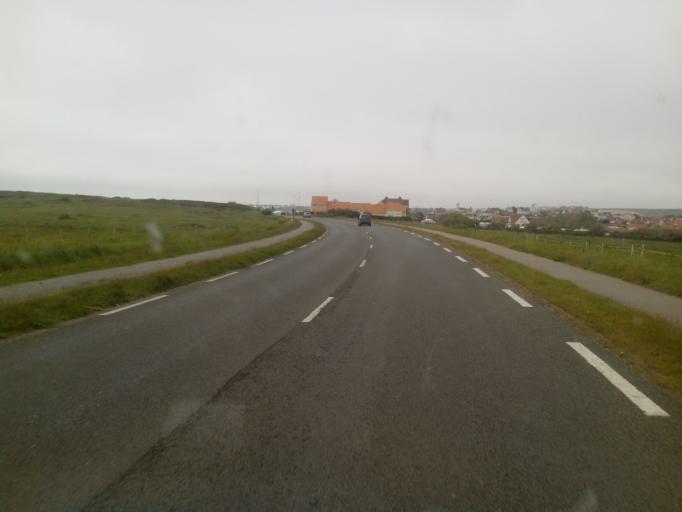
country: FR
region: Nord-Pas-de-Calais
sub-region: Departement du Pas-de-Calais
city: Wimereux
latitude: 50.7578
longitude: 1.6055
